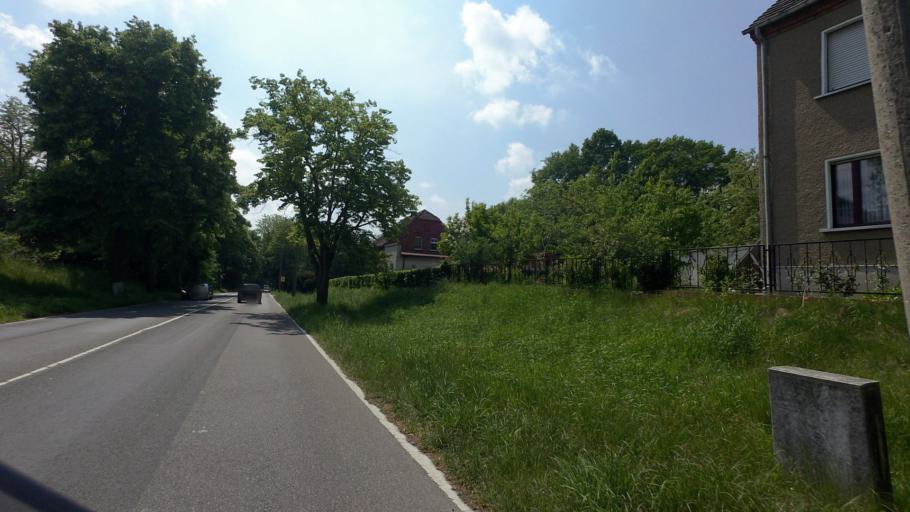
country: DE
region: Brandenburg
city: Spremberg
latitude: 51.5894
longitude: 14.3614
